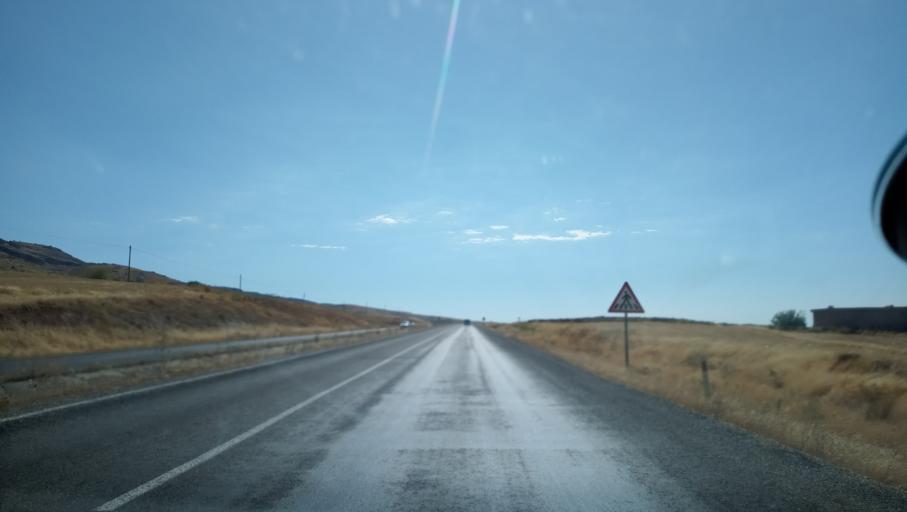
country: TR
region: Diyarbakir
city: Silvan
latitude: 38.1280
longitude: 41.0643
